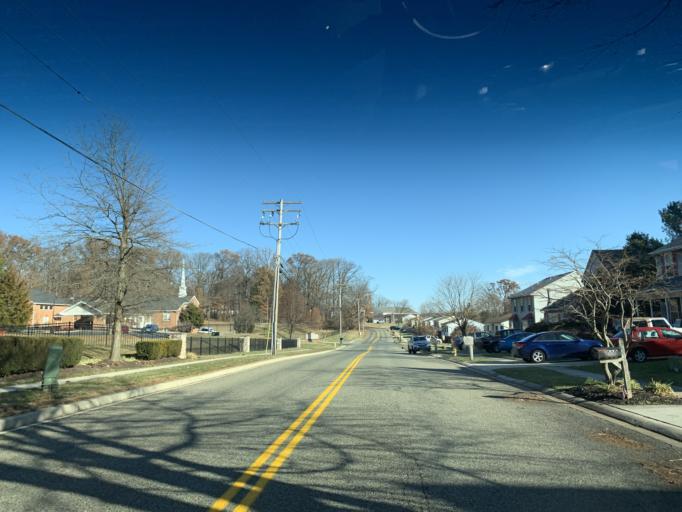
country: US
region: Maryland
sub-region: Harford County
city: Bel Air South
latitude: 39.4893
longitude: -76.3152
